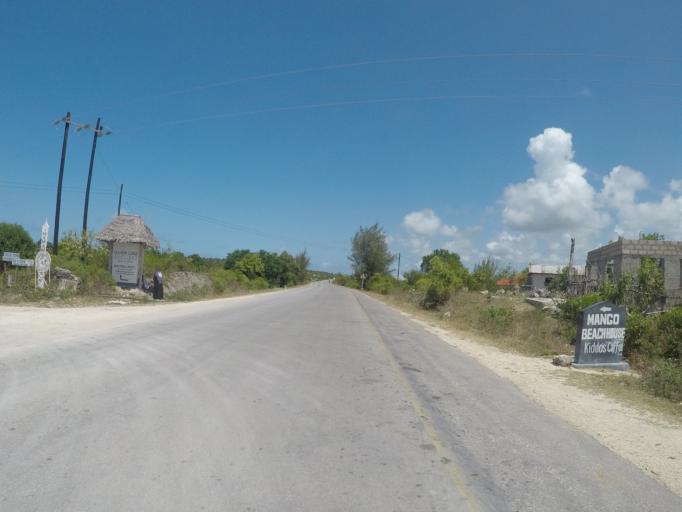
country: TZ
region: Zanzibar Central/South
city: Nganane
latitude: -6.3051
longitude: 39.5393
